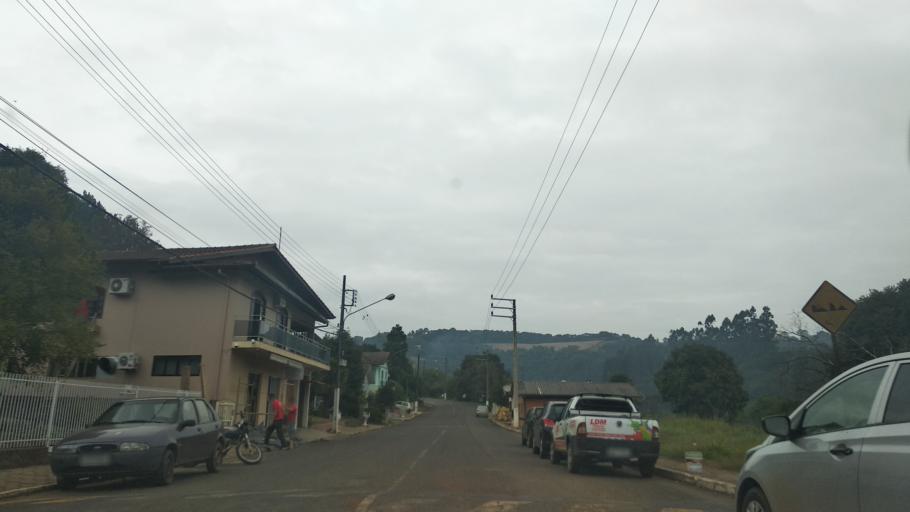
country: BR
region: Santa Catarina
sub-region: Videira
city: Videira
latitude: -27.0540
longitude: -51.2306
